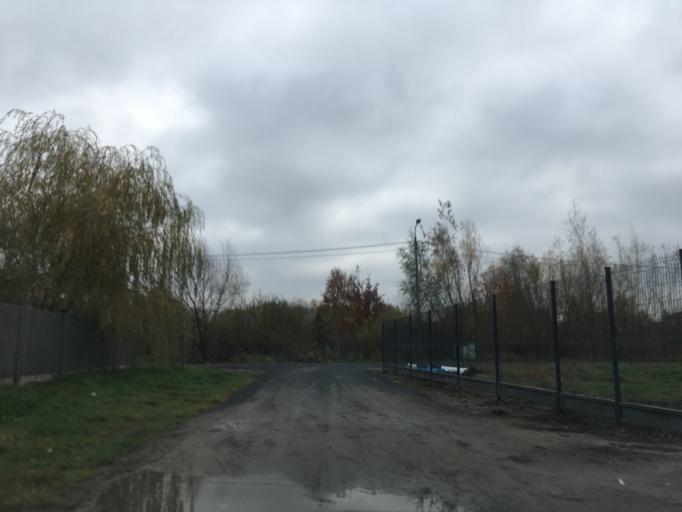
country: PL
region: Masovian Voivodeship
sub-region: Powiat pruszkowski
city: Brwinow
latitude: 52.1424
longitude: 20.7386
